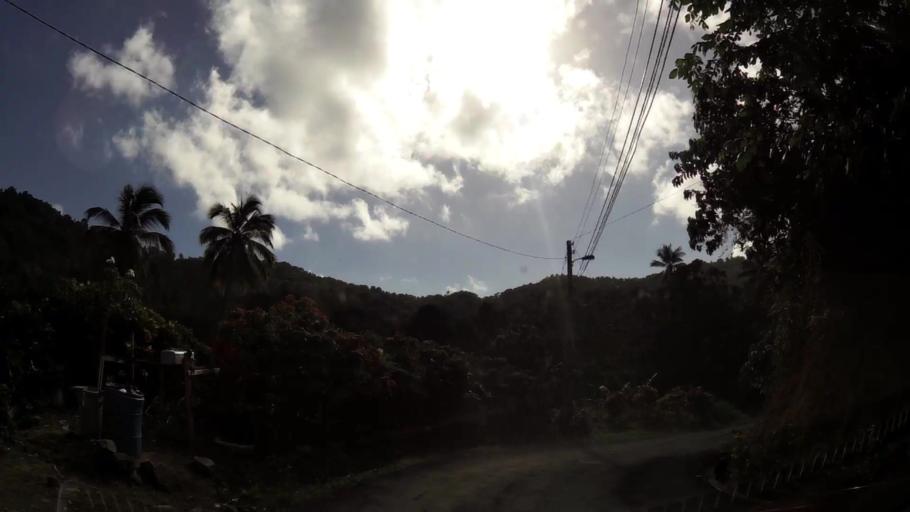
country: DM
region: Saint Andrew
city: Marigot
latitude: 15.5149
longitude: -61.2711
